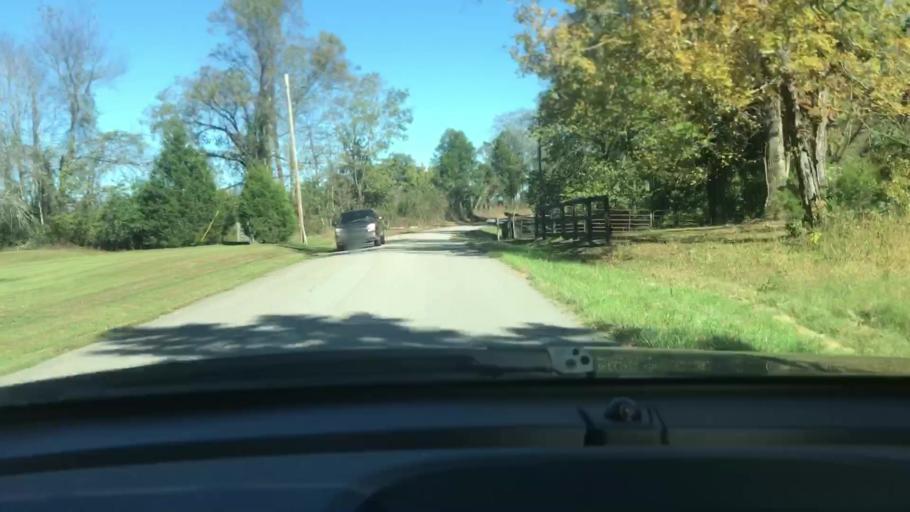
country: US
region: Tennessee
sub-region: Dickson County
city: Charlotte
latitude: 36.1801
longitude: -87.2909
